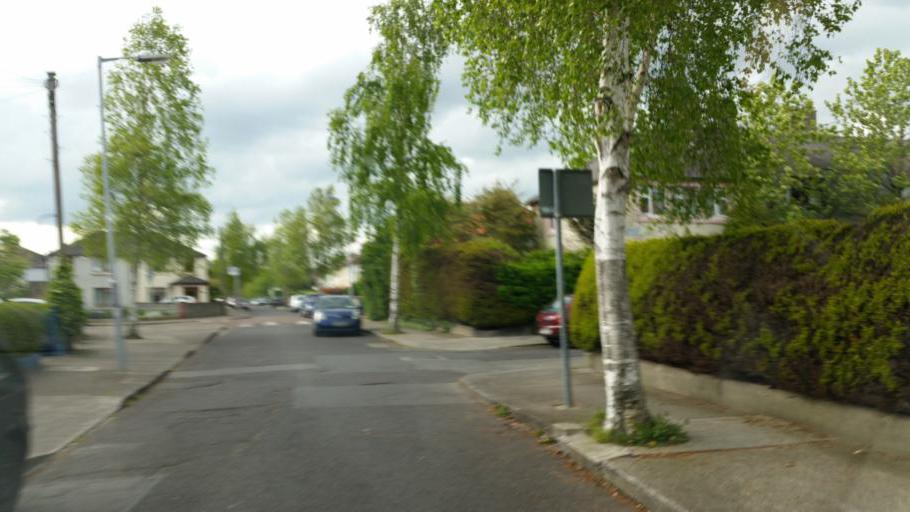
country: IE
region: Leinster
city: Marino
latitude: 53.3687
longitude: -6.2322
